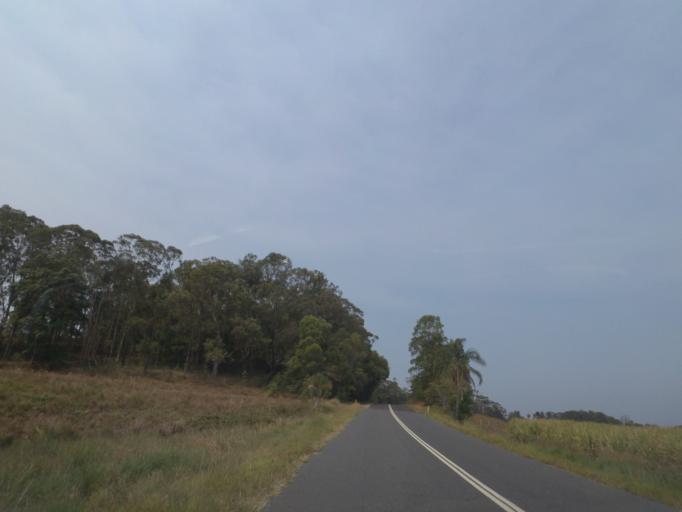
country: AU
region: New South Wales
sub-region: Tweed
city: Burringbar
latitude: -28.4540
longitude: 153.5304
